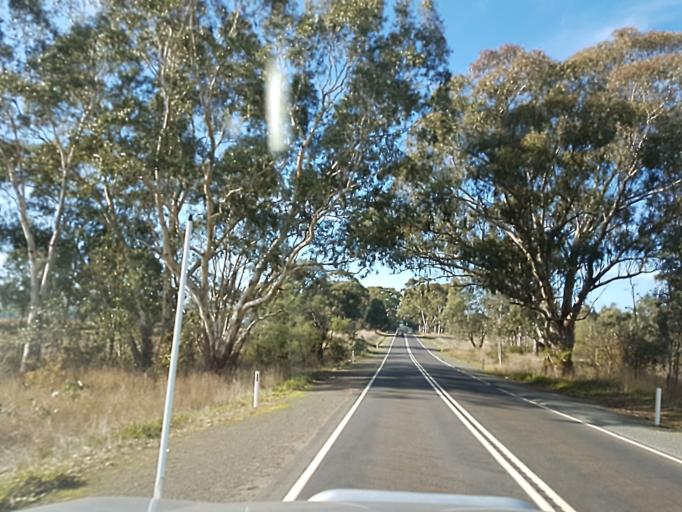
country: AU
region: Victoria
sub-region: Murrindindi
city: Alexandra
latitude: -37.1482
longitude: 145.6090
